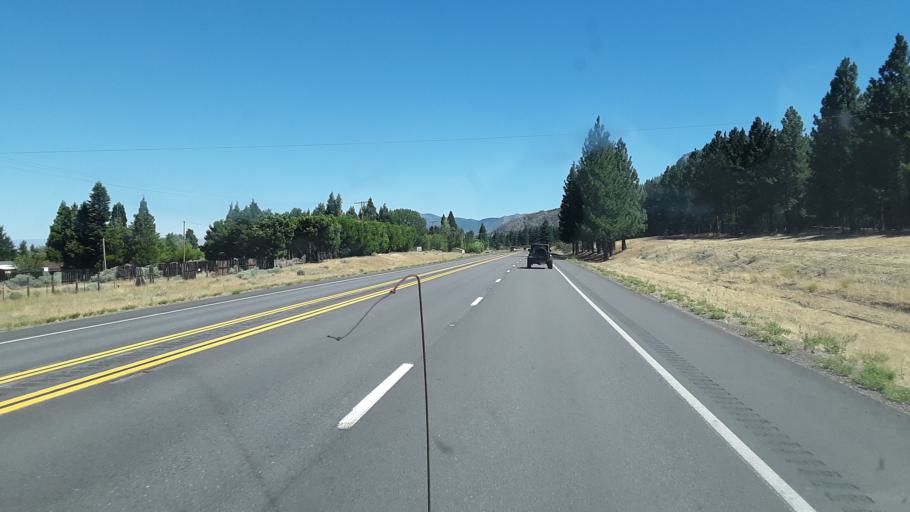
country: US
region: California
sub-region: Lassen County
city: Janesville
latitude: 40.2523
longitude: -120.4634
